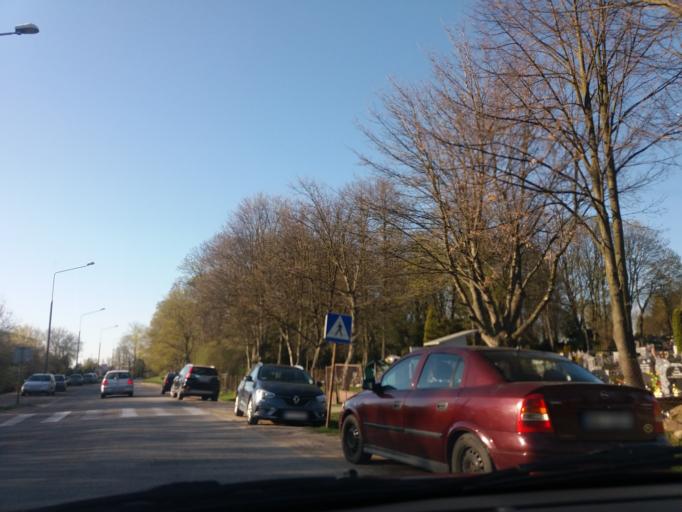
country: PL
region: Warmian-Masurian Voivodeship
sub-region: Powiat nidzicki
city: Nidzica
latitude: 53.3487
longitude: 20.4307
